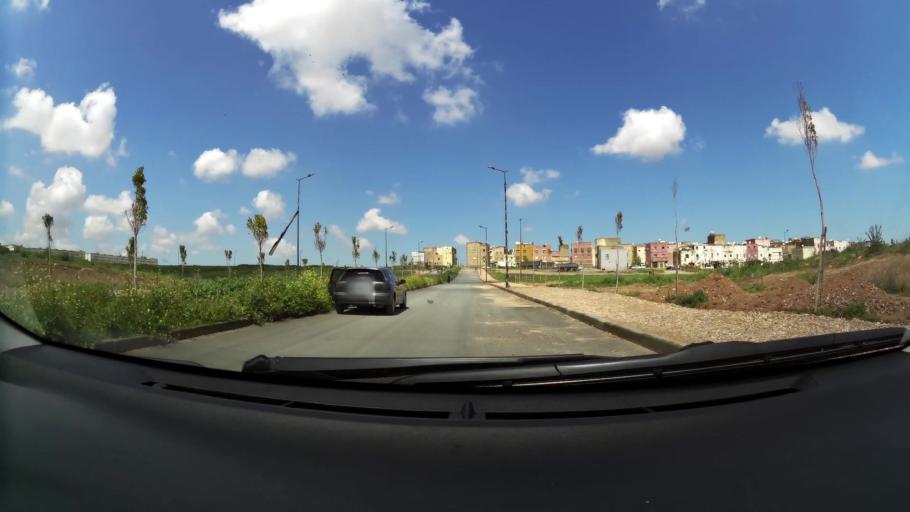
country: MA
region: Grand Casablanca
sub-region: Mediouna
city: Tit Mellil
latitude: 33.5411
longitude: -7.5460
